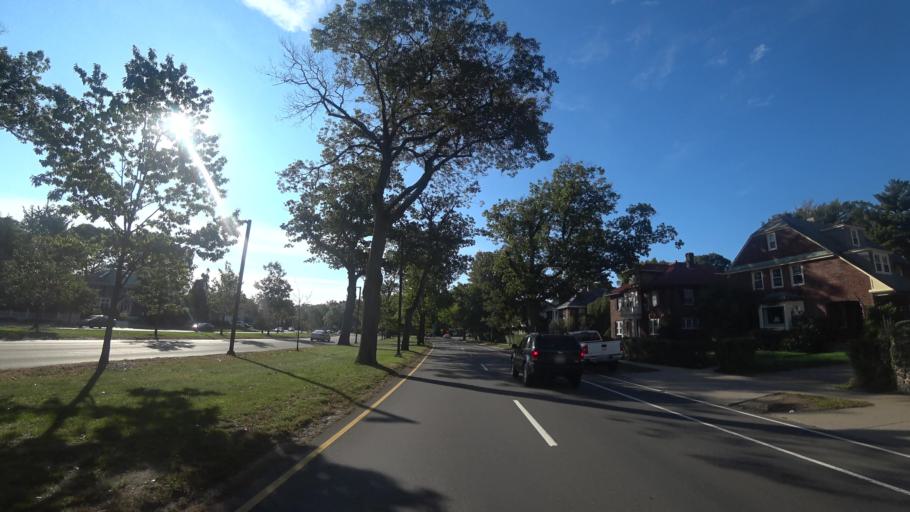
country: US
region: Massachusetts
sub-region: Suffolk County
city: Jamaica Plain
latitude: 42.3110
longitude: -71.1226
